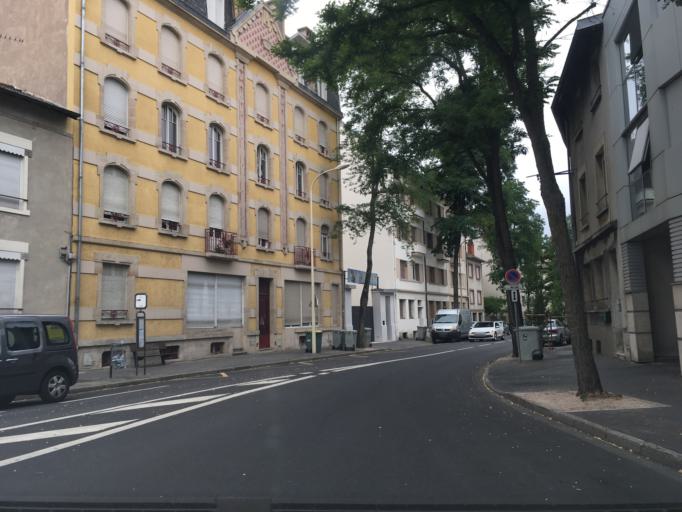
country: FR
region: Lorraine
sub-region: Departement de Meurthe-et-Moselle
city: Nancy
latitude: 48.6966
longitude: 6.1929
